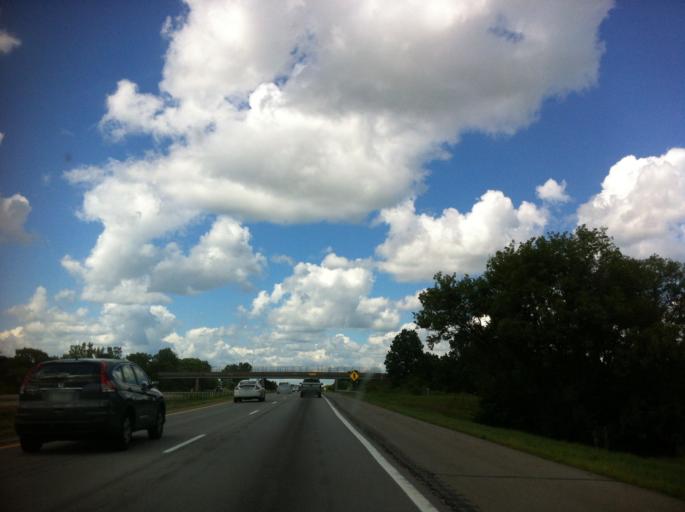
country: US
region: Michigan
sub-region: Washtenaw County
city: Milan
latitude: 42.1540
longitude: -83.6838
